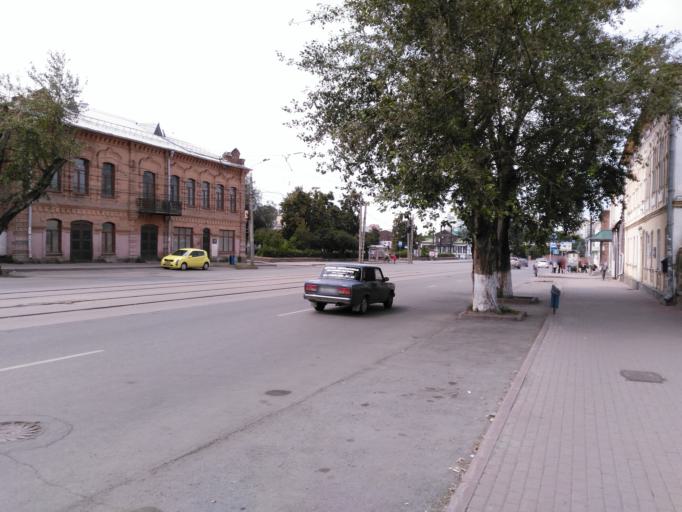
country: RU
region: Chelyabinsk
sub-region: Gorod Chelyabinsk
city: Chelyabinsk
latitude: 55.1661
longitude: 61.4039
